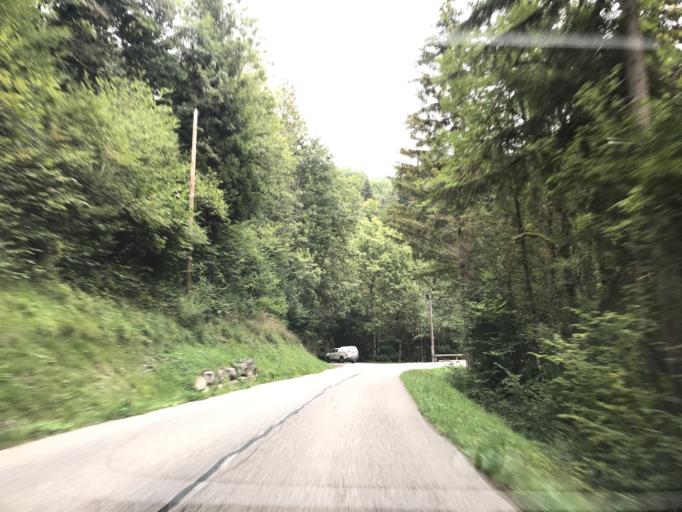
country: FR
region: Rhone-Alpes
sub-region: Departement de la Haute-Savoie
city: Talloires
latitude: 45.8331
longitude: 6.2406
